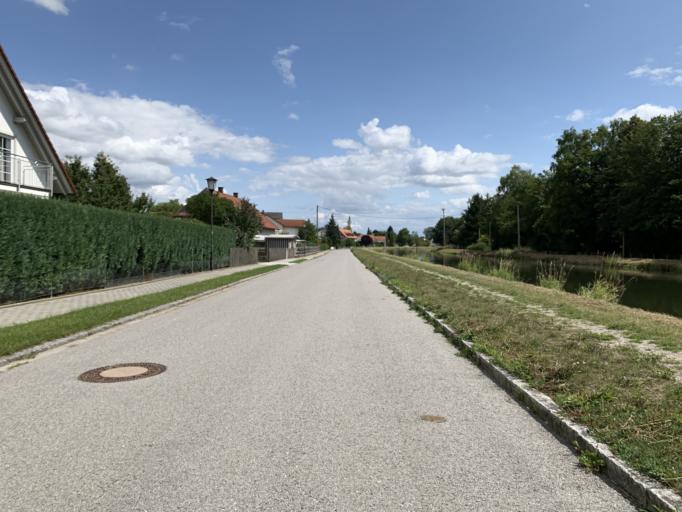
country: DE
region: Bavaria
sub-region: Upper Bavaria
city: Zolling
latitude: 48.4497
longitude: 11.7596
